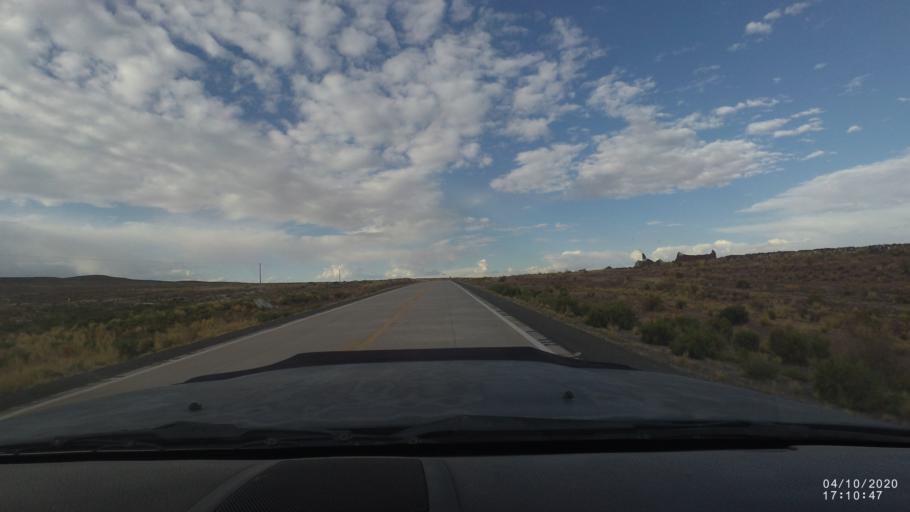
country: BO
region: Oruro
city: Oruro
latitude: -18.3272
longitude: -67.5812
